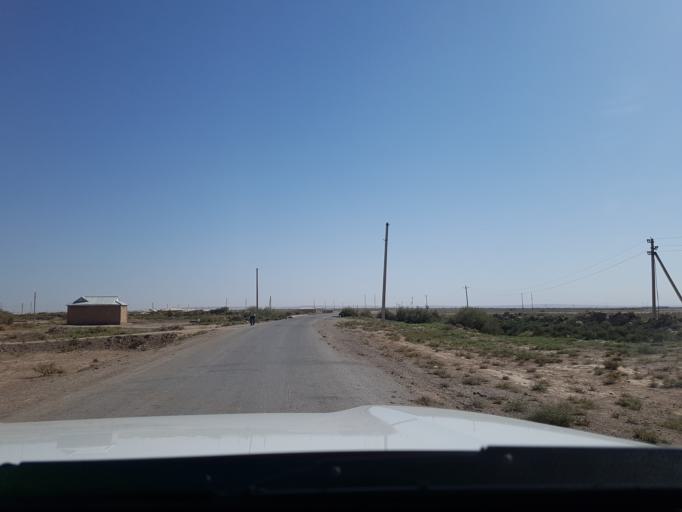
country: IR
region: Razavi Khorasan
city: Sarakhs
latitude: 36.5148
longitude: 61.2527
